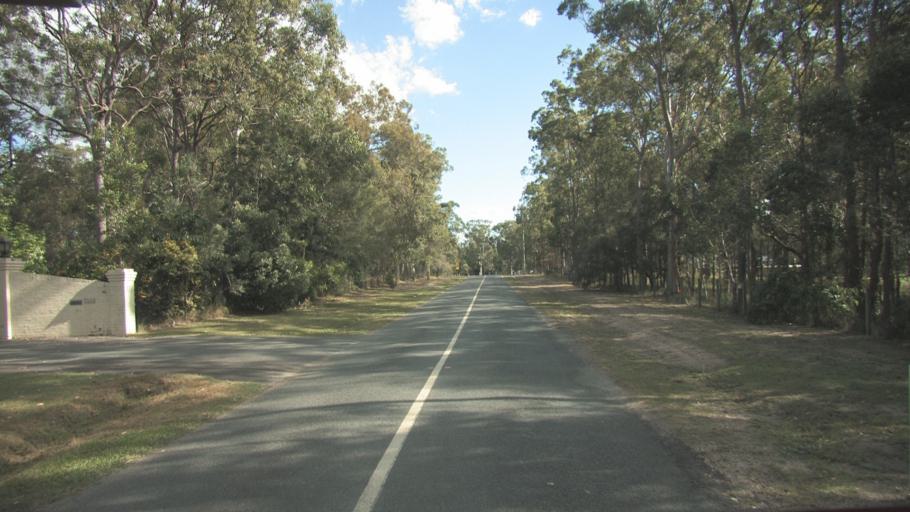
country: AU
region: Queensland
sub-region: Gold Coast
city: Yatala
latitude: -27.6578
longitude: 153.2438
